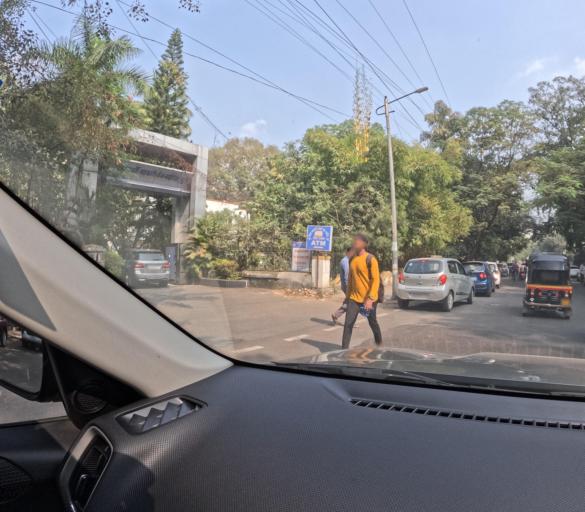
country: IN
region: Maharashtra
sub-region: Pune Division
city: Pune
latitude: 18.5247
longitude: 73.8738
